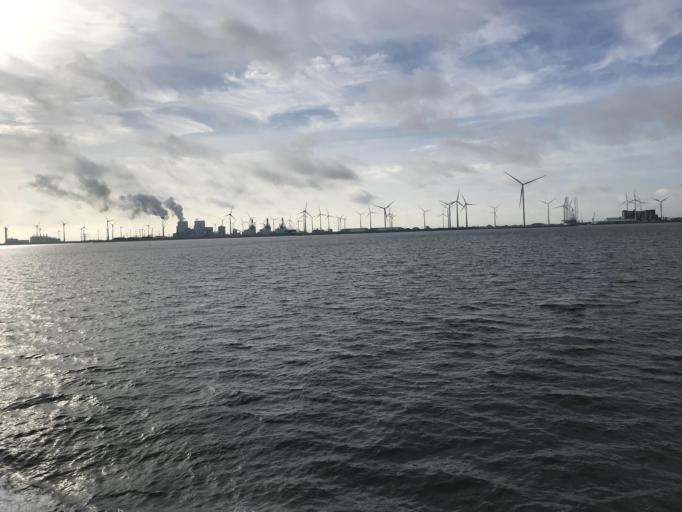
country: NL
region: Groningen
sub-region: Gemeente Appingedam
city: Appingedam
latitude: 53.4741
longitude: 6.8553
